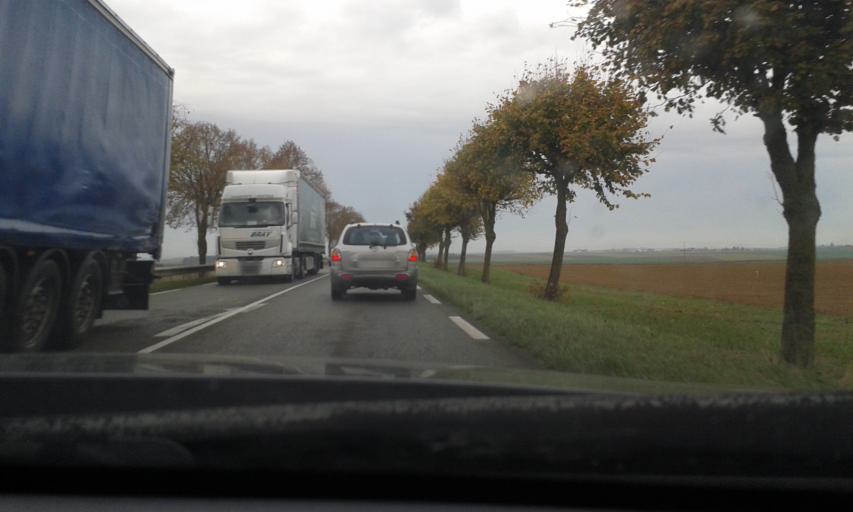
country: FR
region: Centre
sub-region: Departement d'Eure-et-Loir
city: Baigneaux
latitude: 48.1499
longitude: 1.8450
